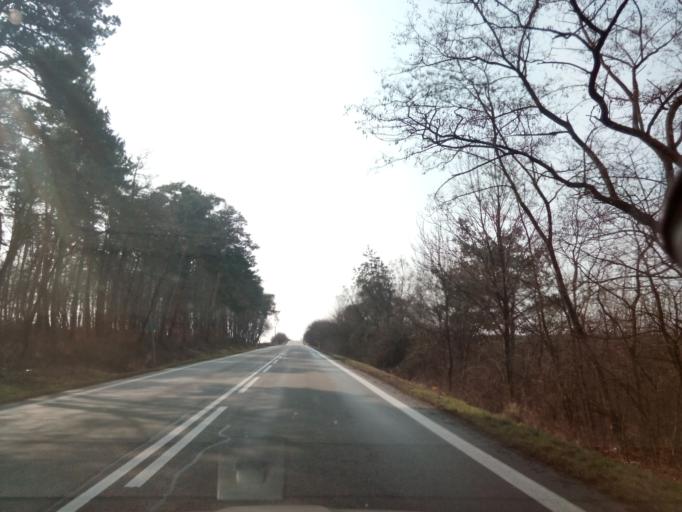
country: HU
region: Borsod-Abauj-Zemplen
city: Satoraljaujhely
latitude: 48.5165
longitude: 21.6590
